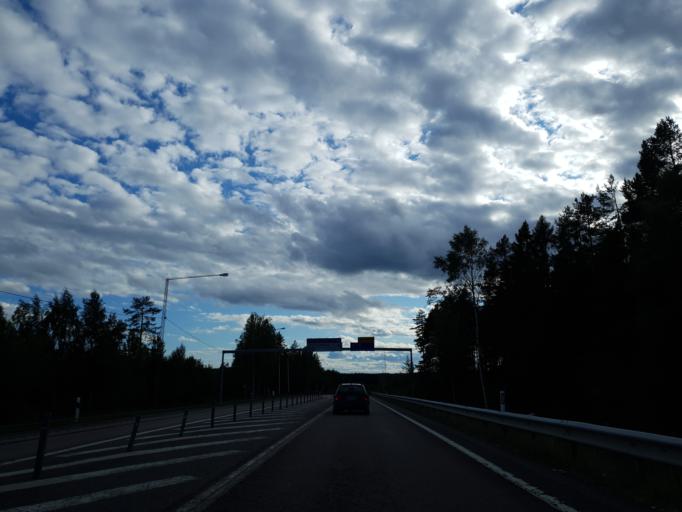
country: SE
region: Vaesternorrland
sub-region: Haernoesands Kommun
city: Haernoesand
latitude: 62.5997
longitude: 17.8104
